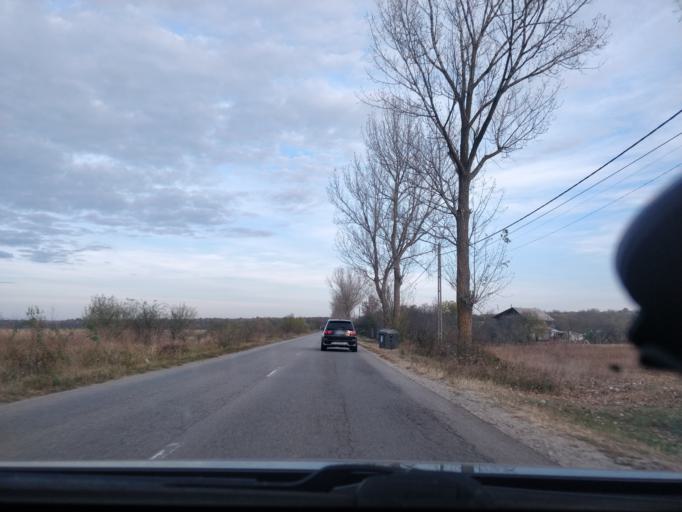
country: RO
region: Giurgiu
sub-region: Comuna Crevedia Mare
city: Crevedia Mare
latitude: 44.4315
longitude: 25.6497
